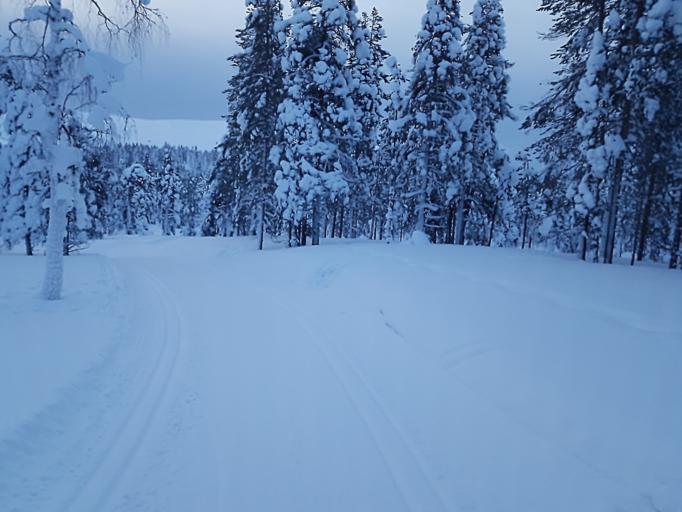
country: FI
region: Lapland
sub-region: Tunturi-Lappi
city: Kolari
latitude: 67.6562
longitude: 24.2465
